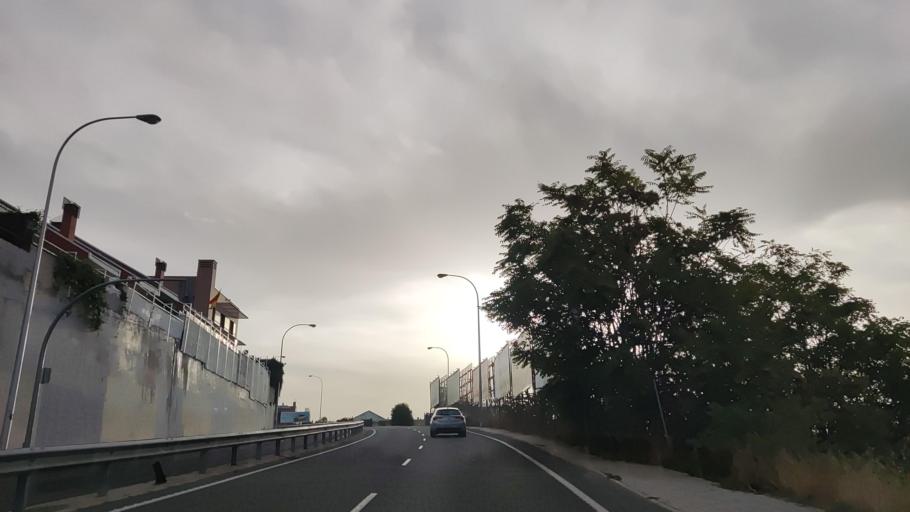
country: ES
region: Madrid
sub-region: Provincia de Madrid
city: Tetuan de las Victorias
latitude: 40.4769
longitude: -3.7346
